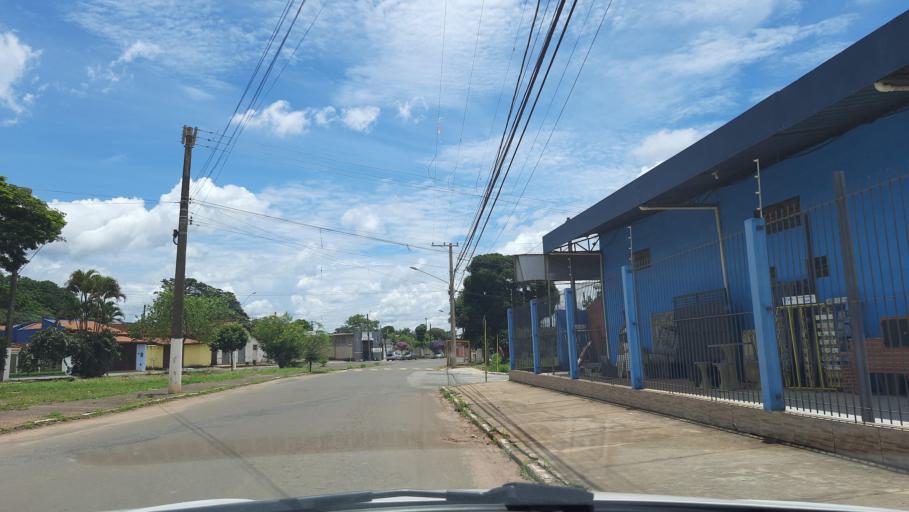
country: BR
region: Sao Paulo
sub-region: Casa Branca
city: Casa Branca
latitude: -21.7834
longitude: -47.0959
